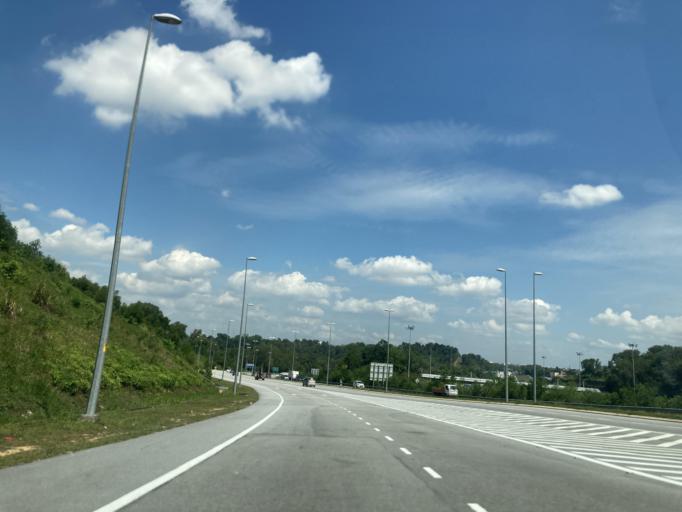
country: MY
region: Selangor
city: Kampung Baru Subang
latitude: 3.1268
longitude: 101.5272
